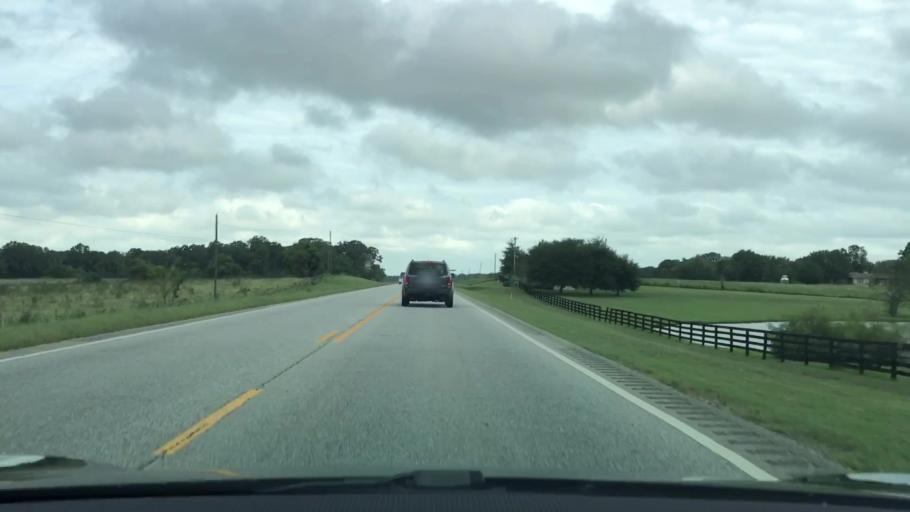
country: US
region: Alabama
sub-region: Montgomery County
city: Pike Road
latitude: 32.3298
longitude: -86.0544
